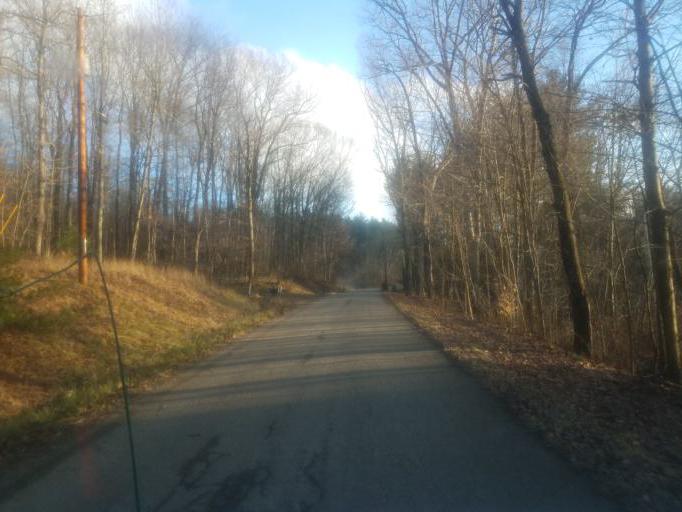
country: US
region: Ohio
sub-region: Sandusky County
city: Bellville
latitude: 40.5950
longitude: -82.3917
